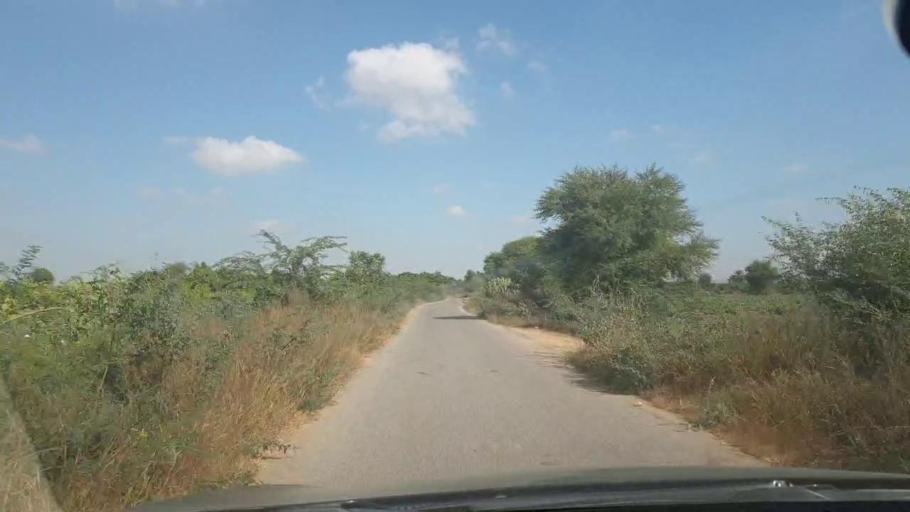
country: PK
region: Sindh
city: Malir Cantonment
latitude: 25.0550
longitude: 67.3896
